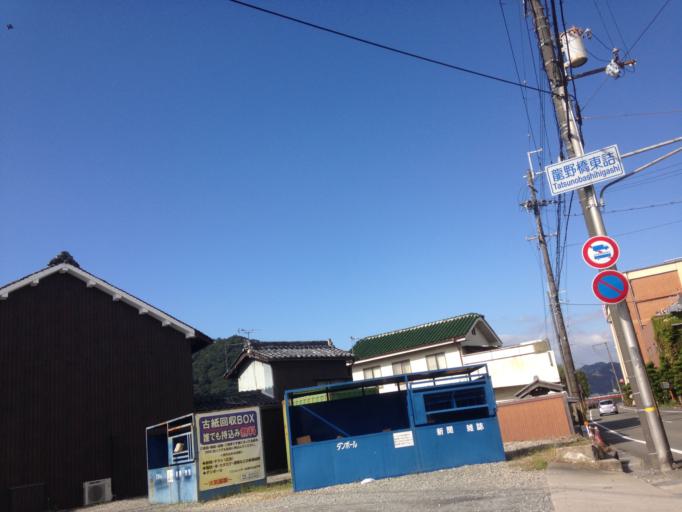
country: JP
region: Hyogo
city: Tatsunocho-tominaga
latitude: 34.8629
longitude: 134.5489
